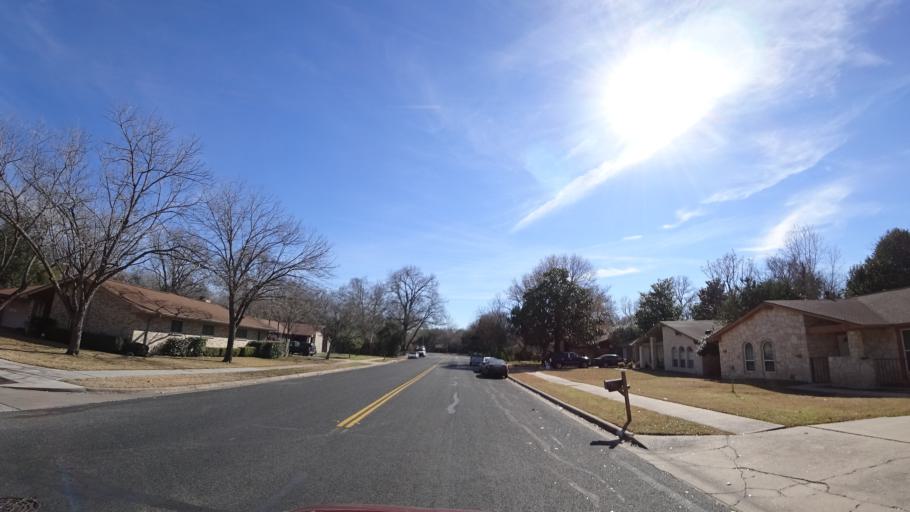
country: US
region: Texas
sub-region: Travis County
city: Wells Branch
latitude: 30.3741
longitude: -97.7042
